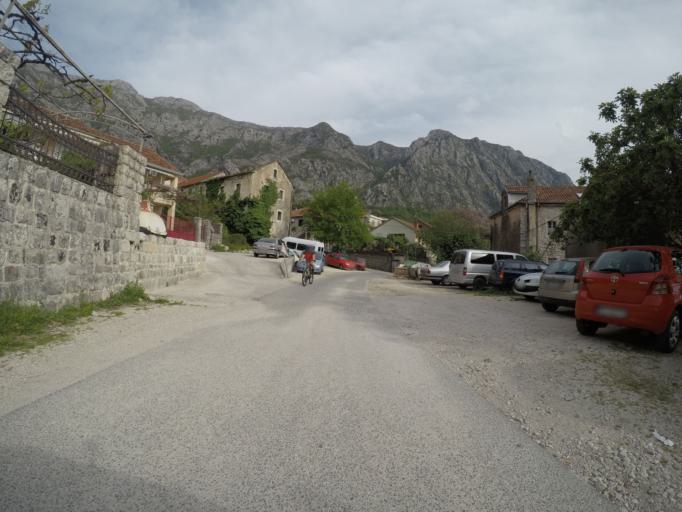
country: ME
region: Kotor
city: Risan
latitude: 42.5151
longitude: 18.6964
